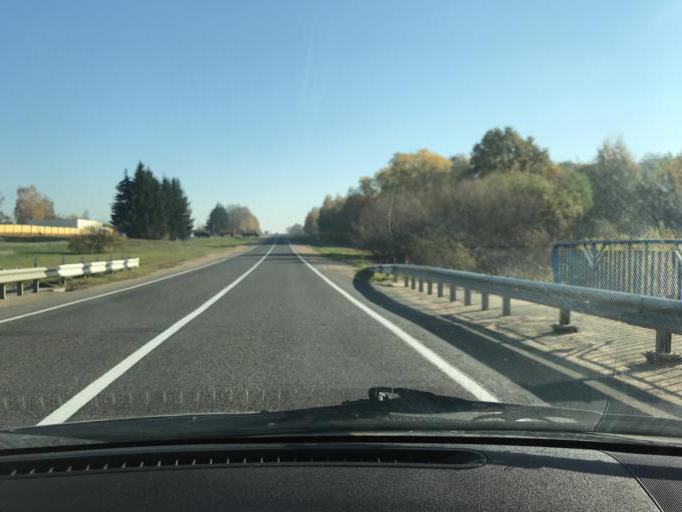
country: BY
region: Minsk
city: Klyetsk
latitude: 52.9658
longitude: 26.5365
